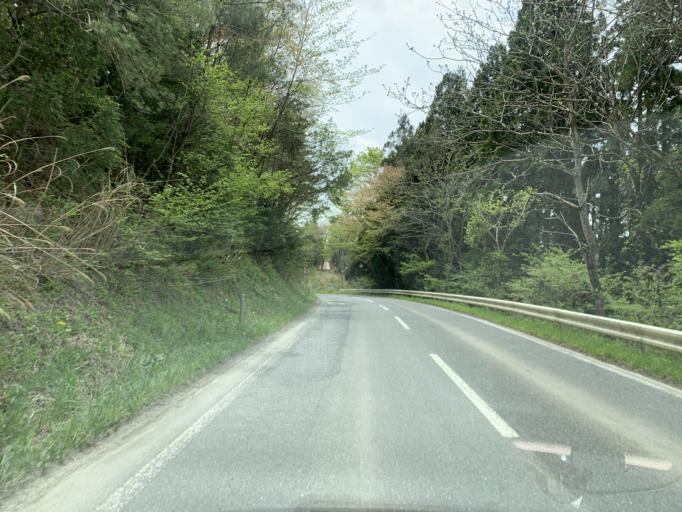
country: JP
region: Iwate
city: Ichinoseki
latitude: 38.7936
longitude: 141.3987
